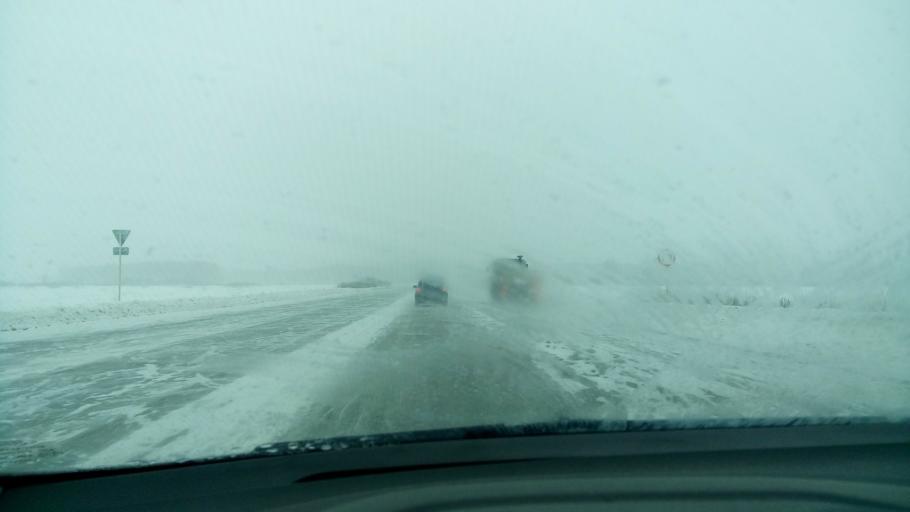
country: RU
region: Sverdlovsk
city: Bogdanovich
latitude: 56.7769
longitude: 61.9952
